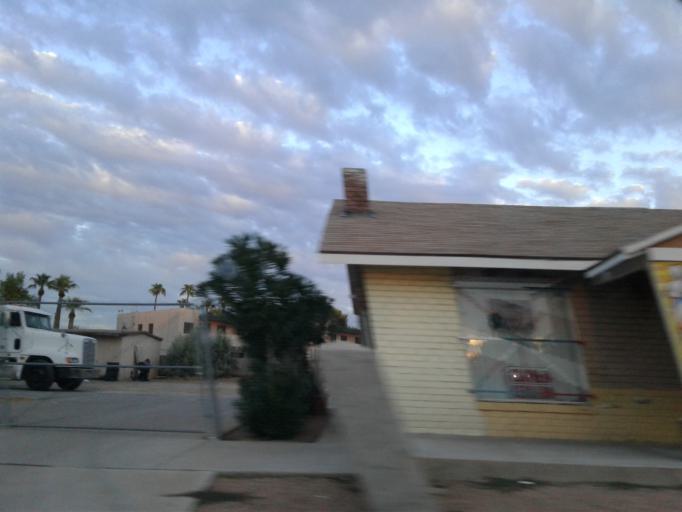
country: US
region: Arizona
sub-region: Maricopa County
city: Phoenix
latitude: 33.4645
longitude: -112.0301
